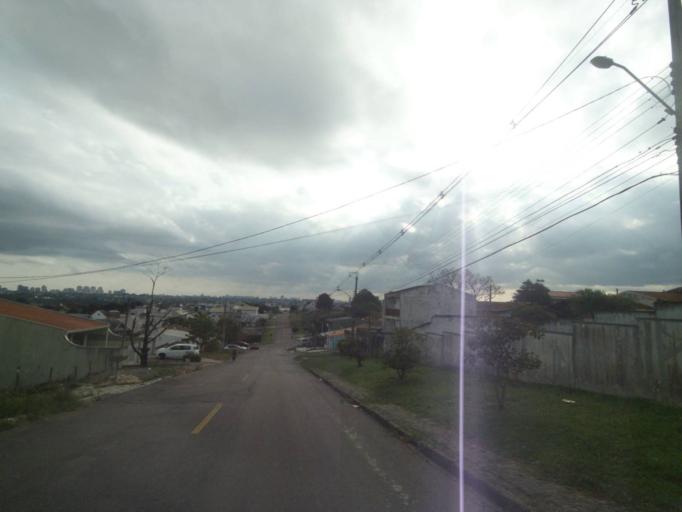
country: BR
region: Parana
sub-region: Pinhais
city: Pinhais
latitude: -25.4096
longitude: -49.2108
